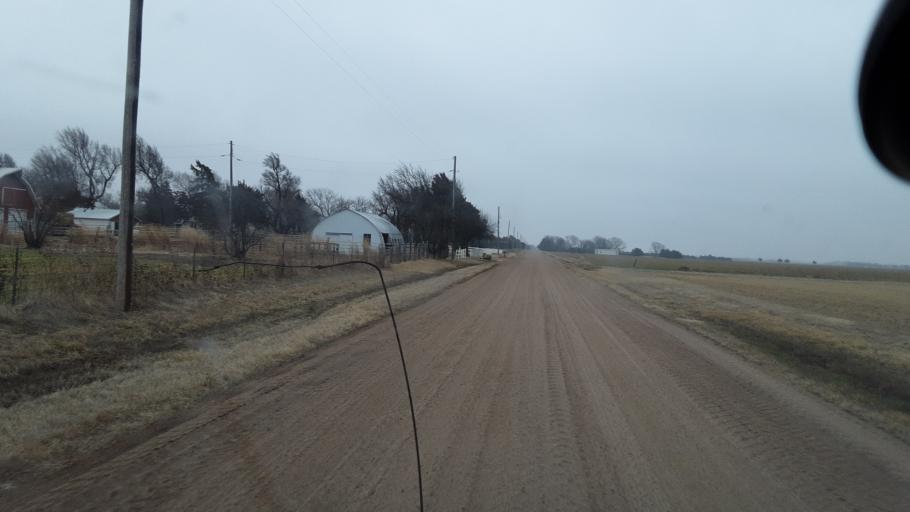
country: US
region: Kansas
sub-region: Reno County
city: South Hutchinson
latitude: 37.9846
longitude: -98.0102
